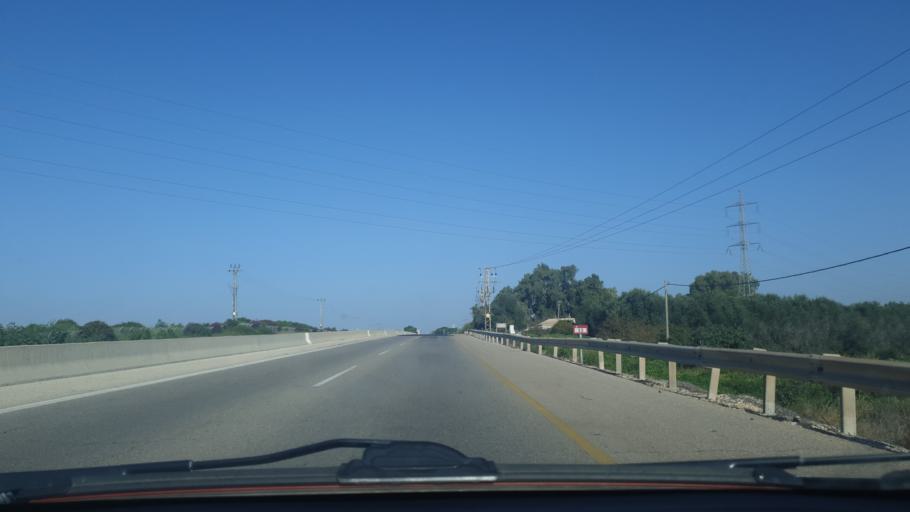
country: IL
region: Central District
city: Bet Dagan
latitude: 31.9845
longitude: 34.8330
